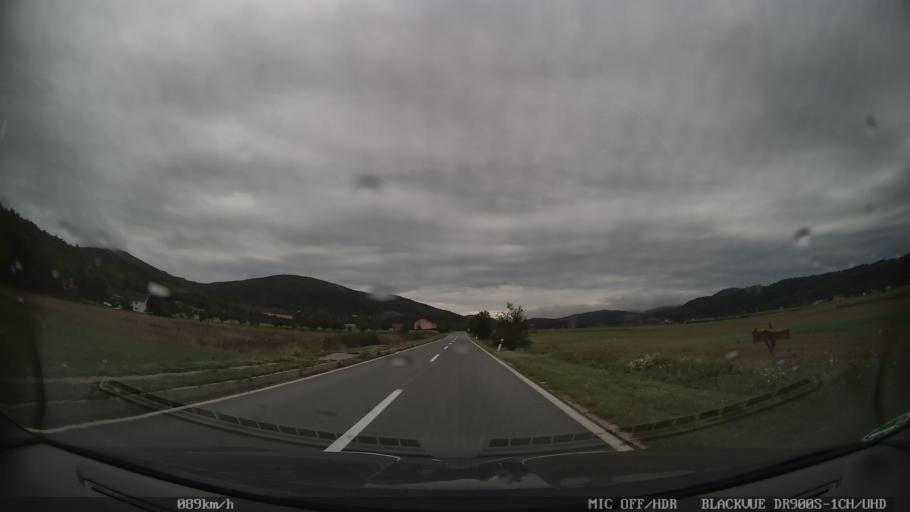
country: HR
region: Licko-Senjska
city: Otocac
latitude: 44.9120
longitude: 15.1626
